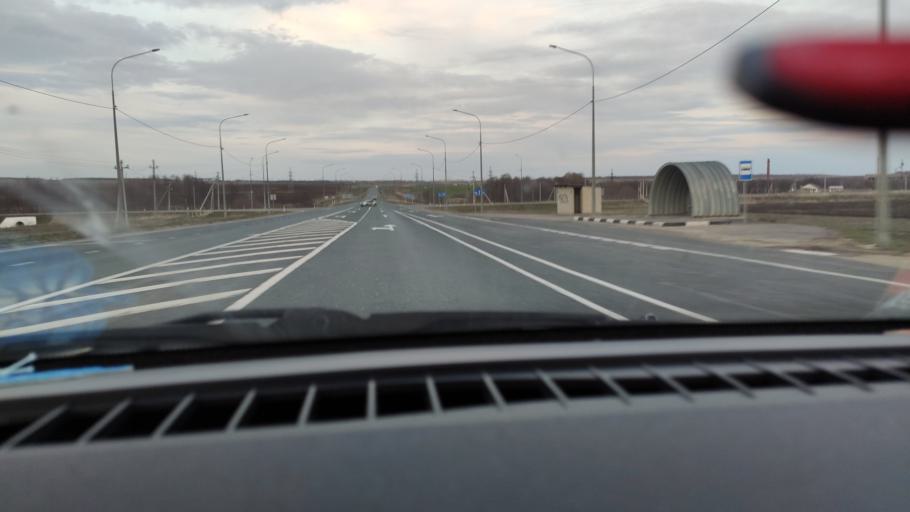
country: RU
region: Saratov
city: Yelshanka
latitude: 51.8272
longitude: 46.3961
